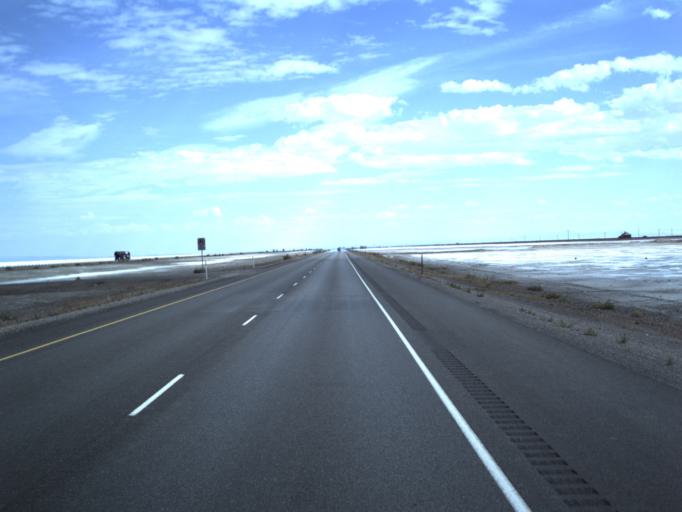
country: US
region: Utah
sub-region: Tooele County
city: Wendover
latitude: 40.7397
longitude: -113.9123
